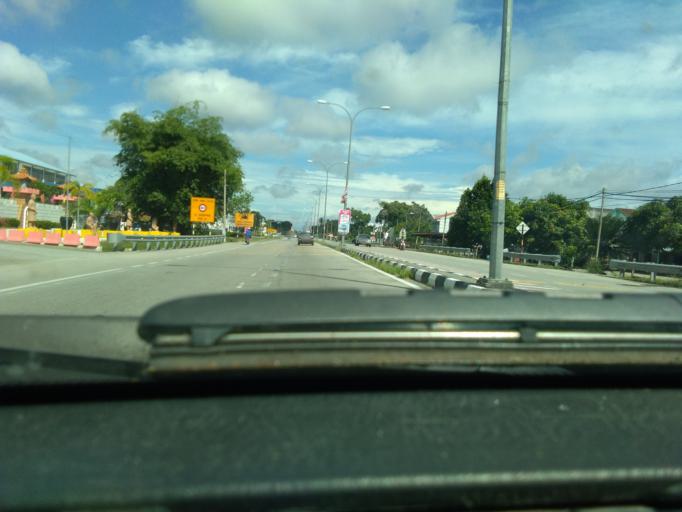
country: MY
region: Perak
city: Bagan Serai
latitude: 5.0050
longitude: 100.5453
